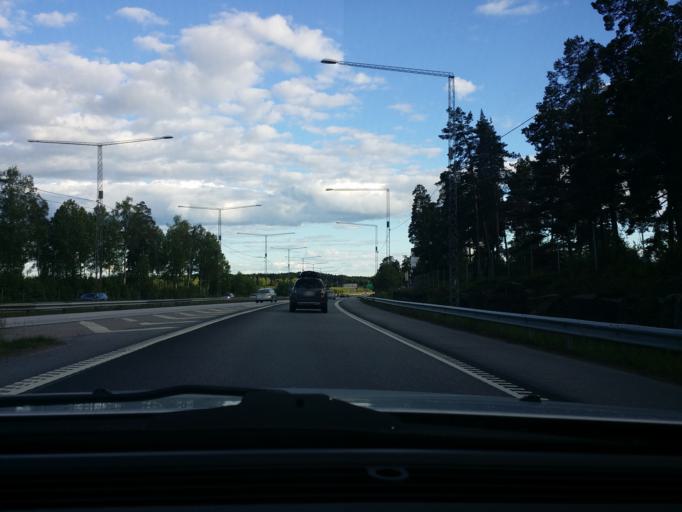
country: SE
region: Stockholm
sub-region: Sigtuna Kommun
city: Rosersberg
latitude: 59.6114
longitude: 17.8988
